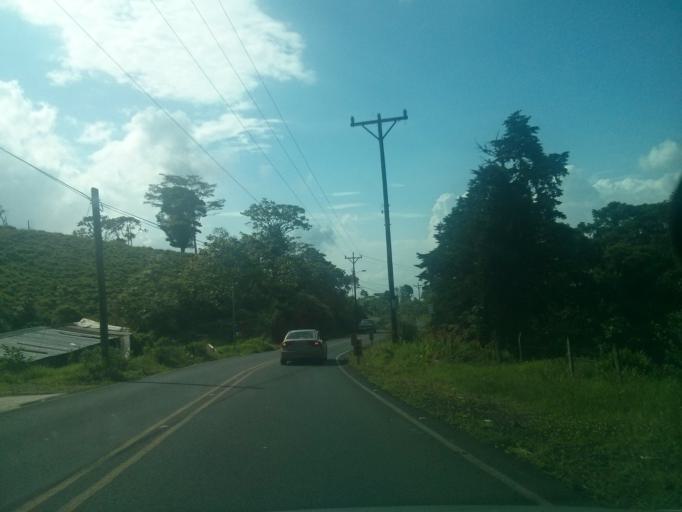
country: CR
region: Heredia
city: Santo Domingo
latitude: 10.1923
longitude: -84.1548
